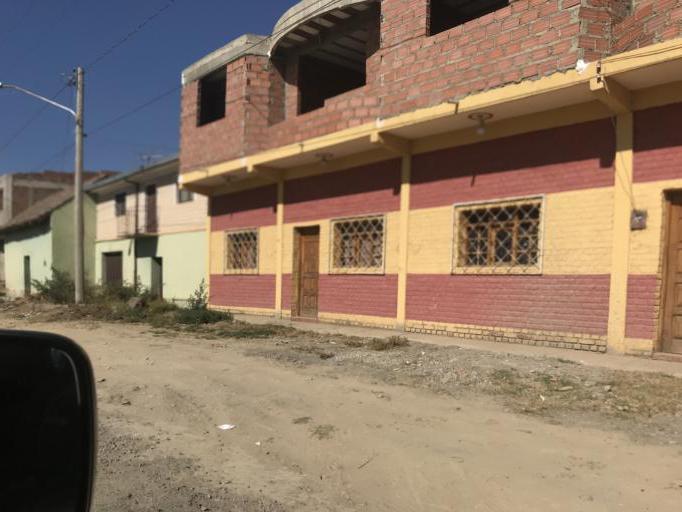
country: BO
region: Cochabamba
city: Punata
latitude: -17.5536
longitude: -65.8545
